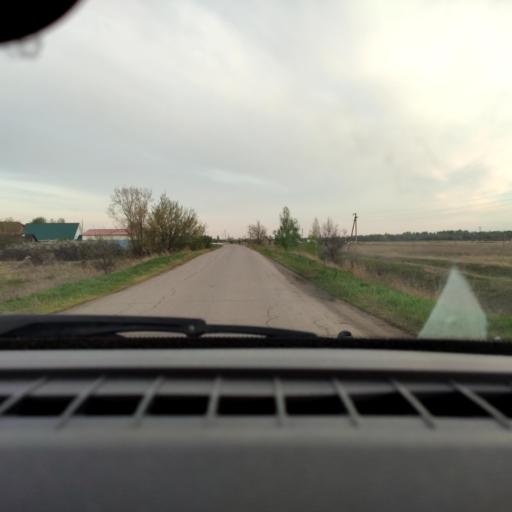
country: RU
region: Samara
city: Georgiyevka
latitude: 53.2723
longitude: 50.9573
